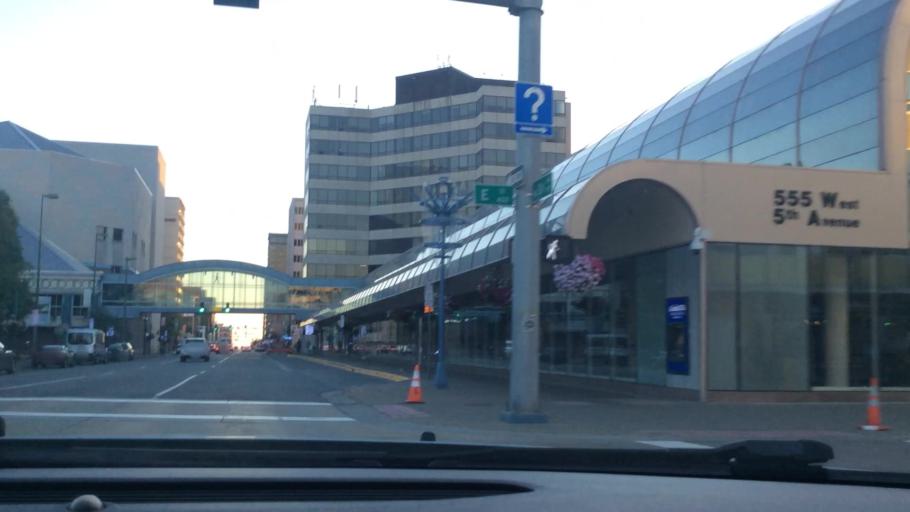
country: US
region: Alaska
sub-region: Anchorage Municipality
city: Anchorage
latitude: 61.2176
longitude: -149.8913
